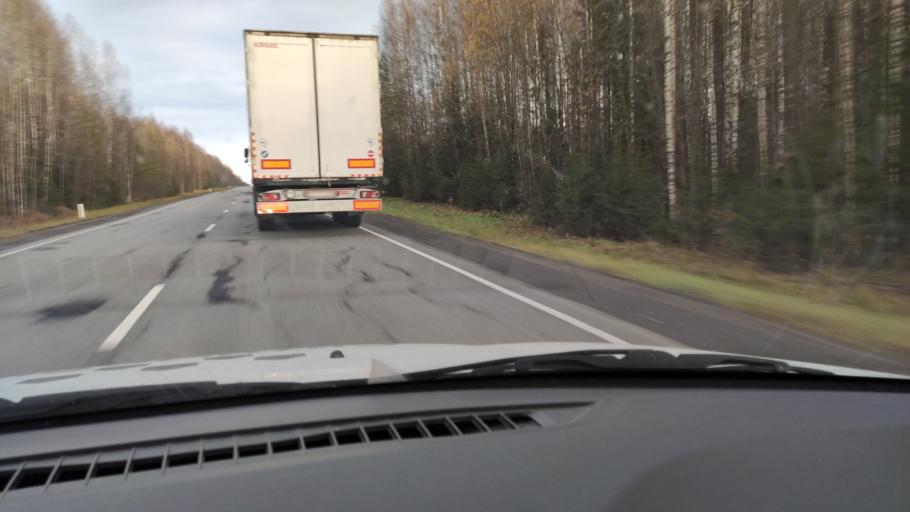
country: RU
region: Kirov
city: Chernaya Kholunitsa
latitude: 58.7709
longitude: 51.9541
